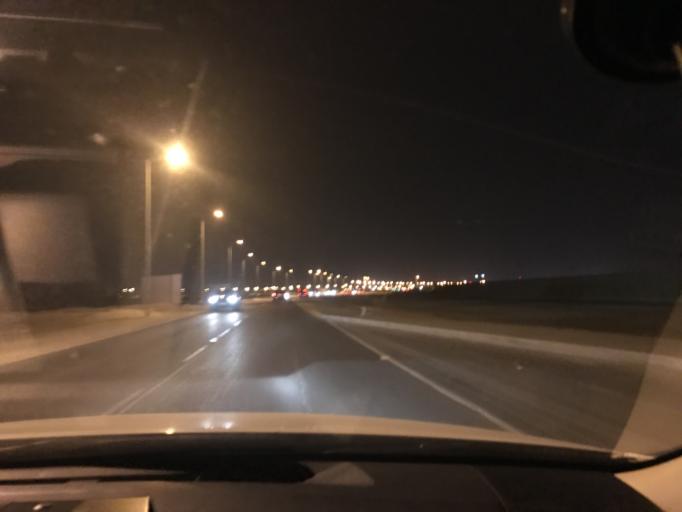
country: BH
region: Muharraq
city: Al Hadd
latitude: 26.2629
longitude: 50.6549
